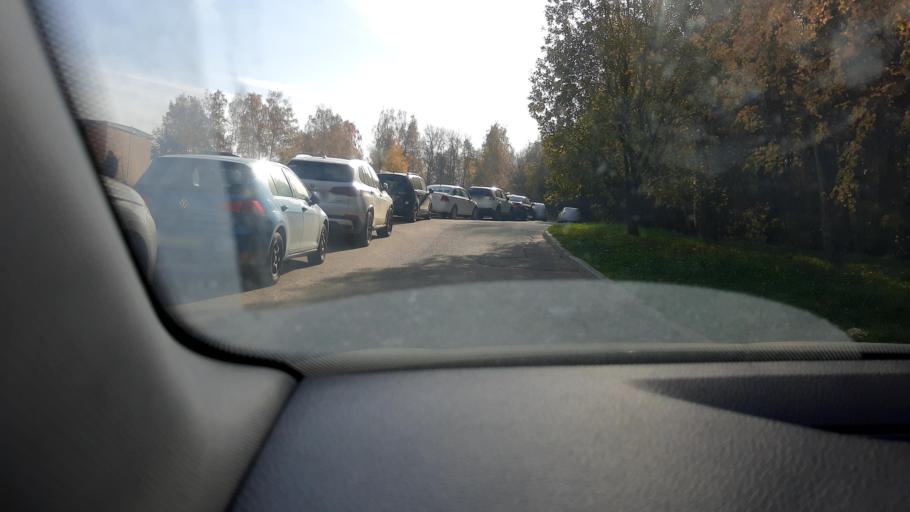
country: RU
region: Moscow
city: Annino
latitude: 55.5591
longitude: 37.5753
